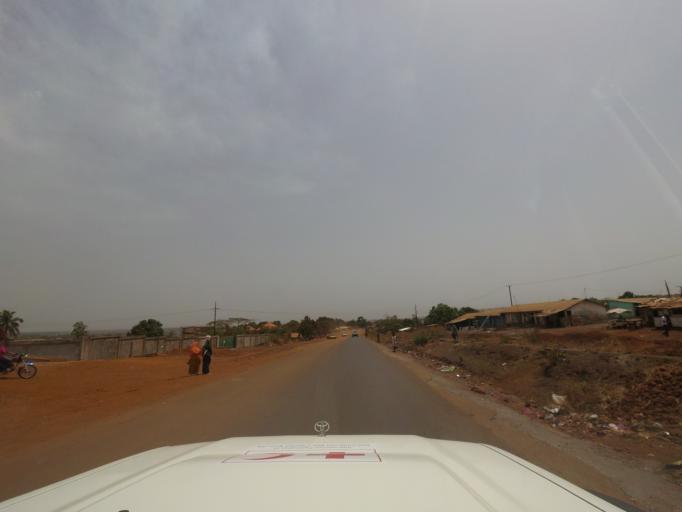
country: GN
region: Kindia
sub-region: Prefecture de Dubreka
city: Dubreka
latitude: 9.7138
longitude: -13.4860
